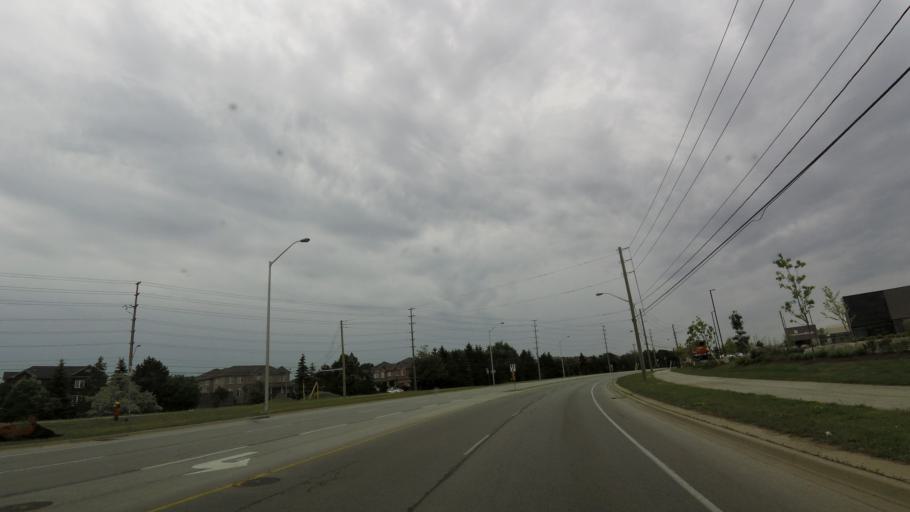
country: CA
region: Ontario
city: Oakville
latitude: 43.3865
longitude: -79.7434
